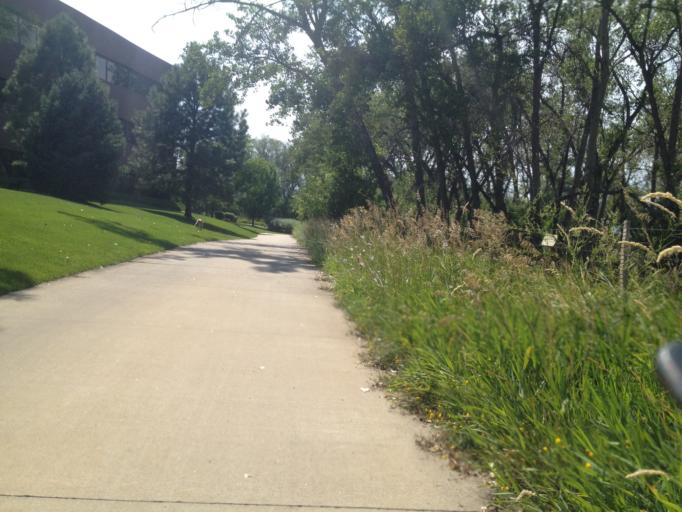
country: US
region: Colorado
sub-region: Boulder County
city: Boulder
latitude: 40.0262
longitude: -105.2232
